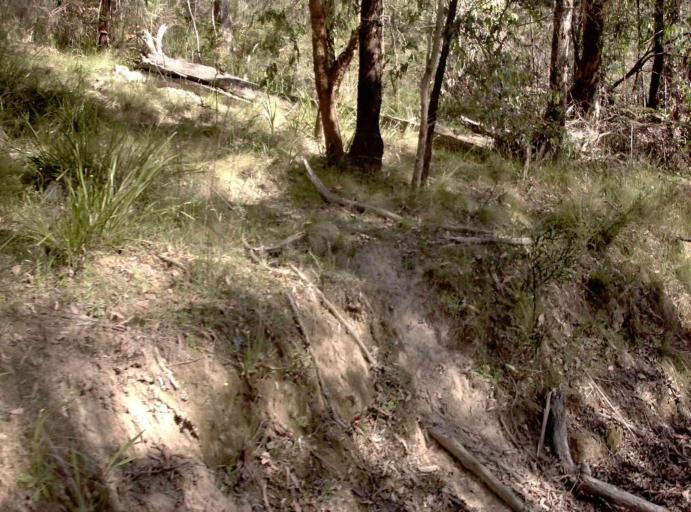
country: AU
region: New South Wales
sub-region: Bombala
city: Bombala
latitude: -37.3802
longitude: 148.6760
